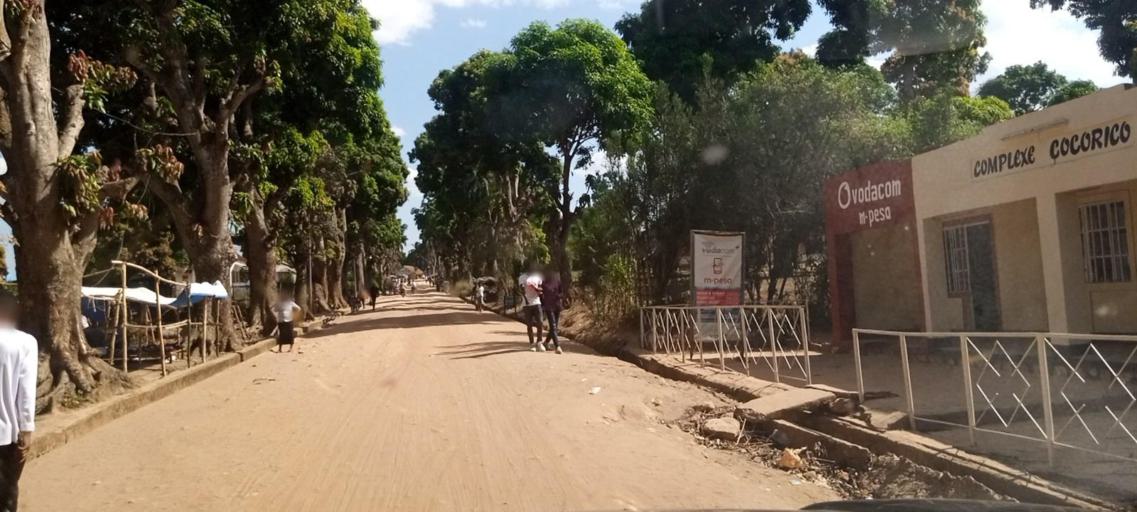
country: CD
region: Kasai-Oriental
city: Kabinda
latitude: -6.1320
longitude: 24.4887
